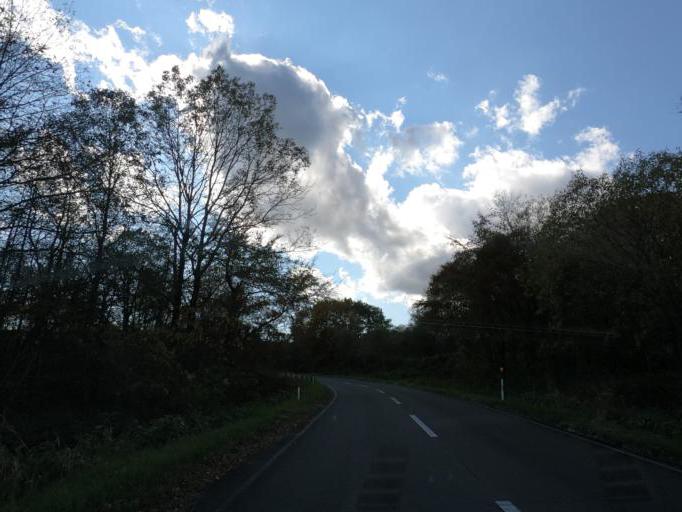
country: JP
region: Hokkaido
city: Otofuke
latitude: 43.2824
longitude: 143.2354
